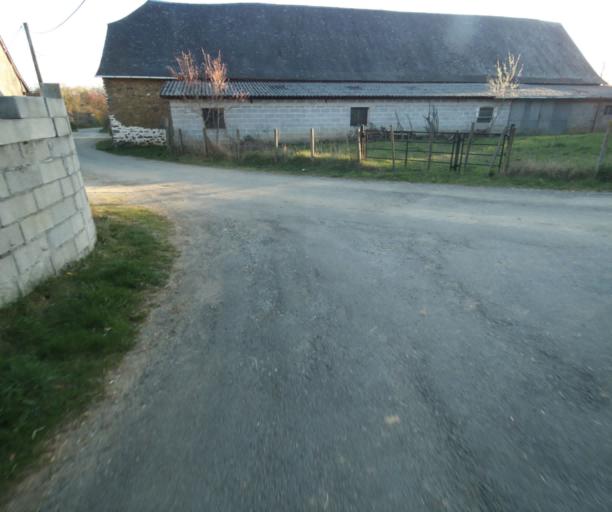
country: FR
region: Limousin
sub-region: Departement de la Correze
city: Uzerche
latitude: 45.3611
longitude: 1.5896
